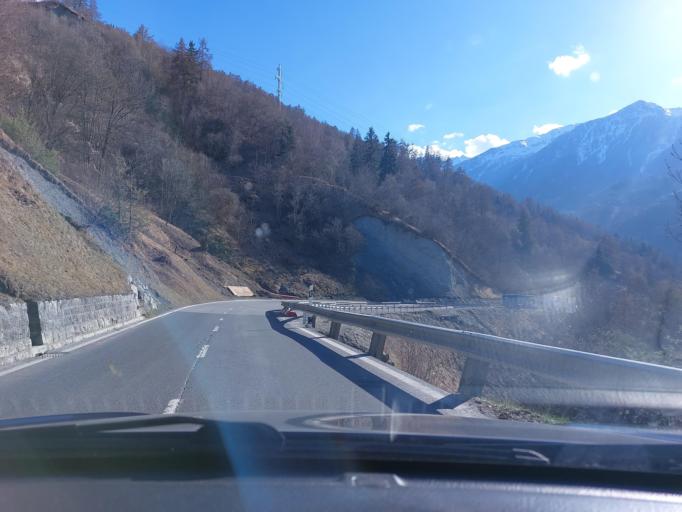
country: CH
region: Valais
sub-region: Herens District
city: Heremence
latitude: 46.1731
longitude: 7.4165
